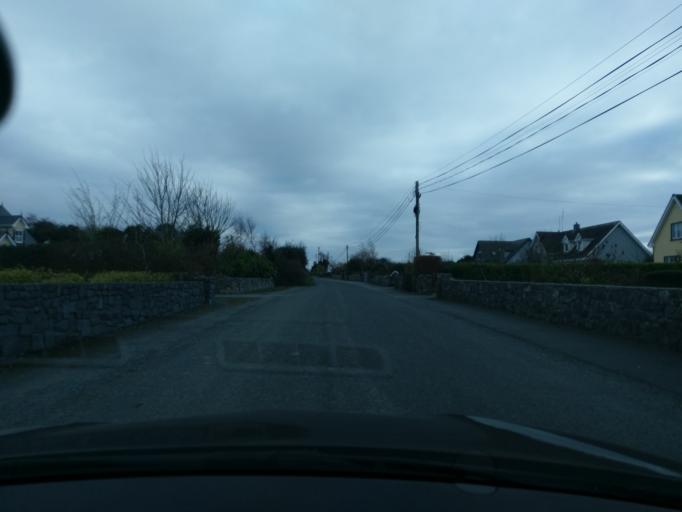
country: IE
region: Connaught
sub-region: County Galway
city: Oranmore
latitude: 53.1898
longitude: -8.9126
